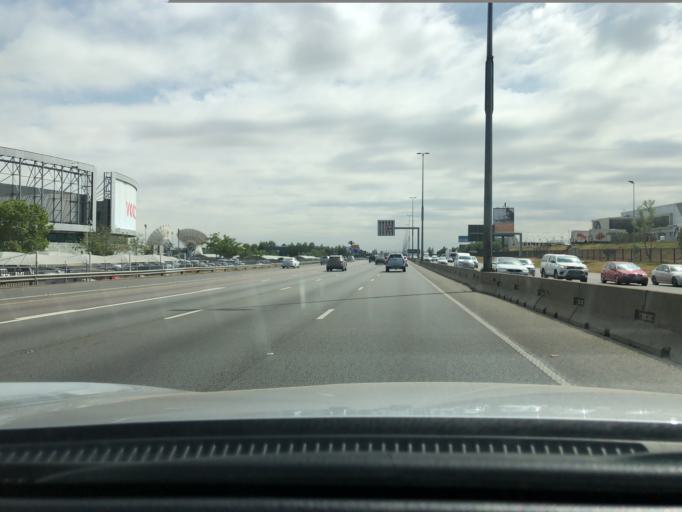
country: ZA
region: Gauteng
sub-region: City of Johannesburg Metropolitan Municipality
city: Midrand
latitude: -25.9760
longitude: 28.1274
